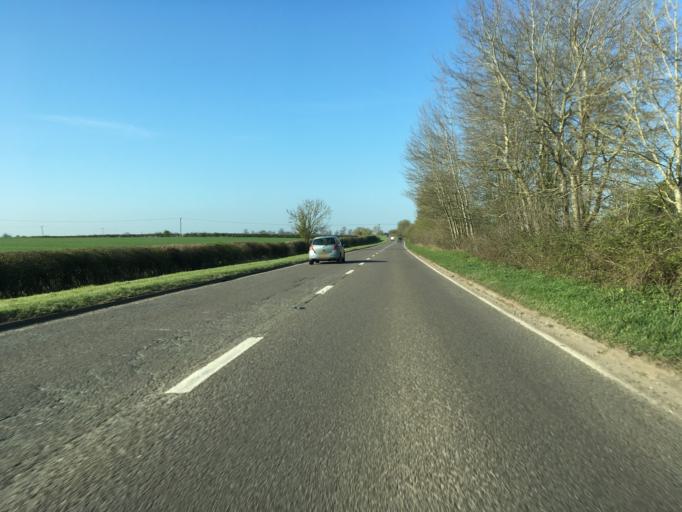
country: GB
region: England
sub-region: Northamptonshire
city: Deanshanger
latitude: 52.0359
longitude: -0.8972
